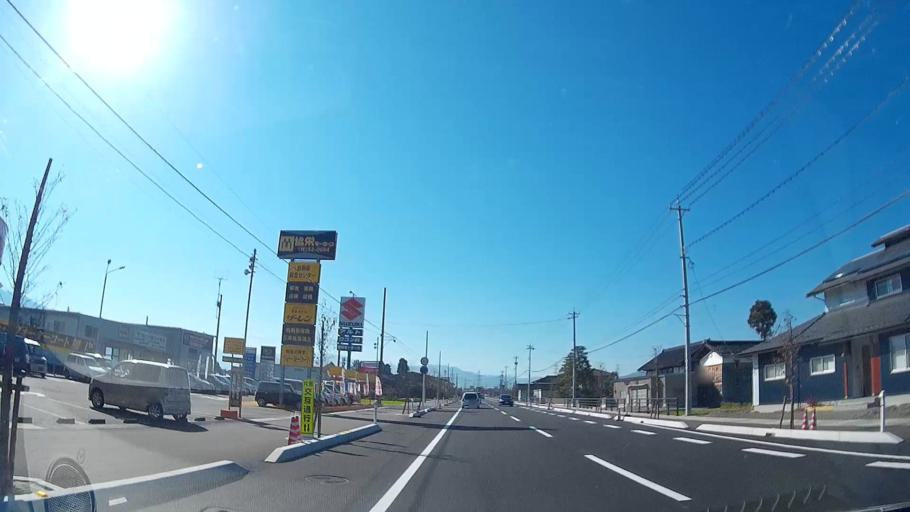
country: JP
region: Toyama
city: Fukumitsu
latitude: 36.5689
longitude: 136.8876
